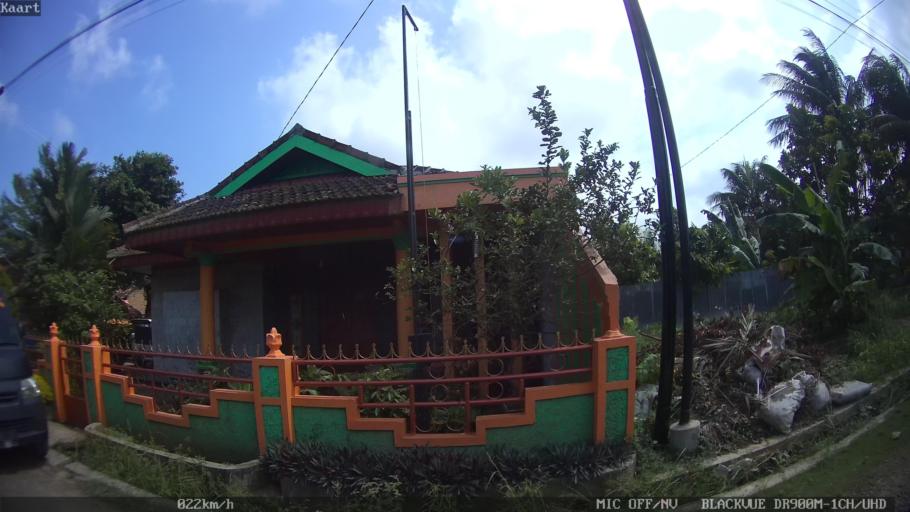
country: ID
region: Lampung
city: Kedaton
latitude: -5.3419
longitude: 105.2910
